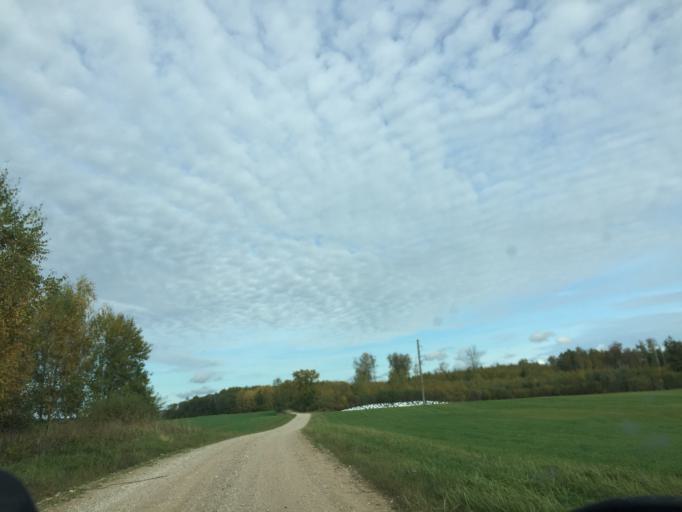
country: LV
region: Jaunpils
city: Jaunpils
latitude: 56.6408
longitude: 23.0754
